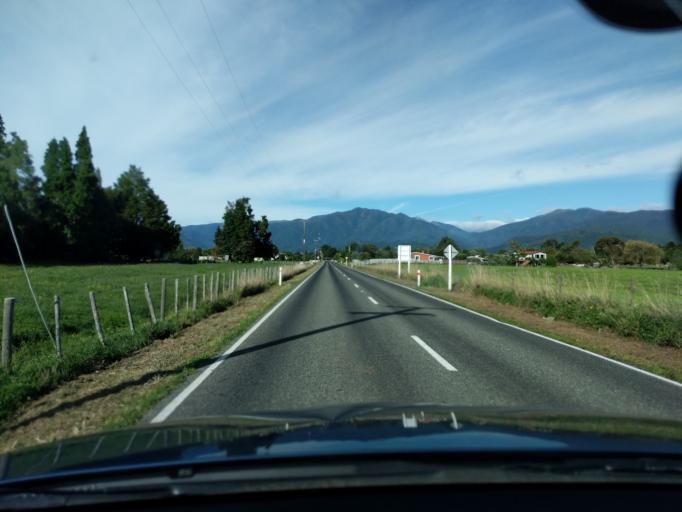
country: NZ
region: Tasman
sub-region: Tasman District
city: Takaka
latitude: -40.8534
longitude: 172.8274
